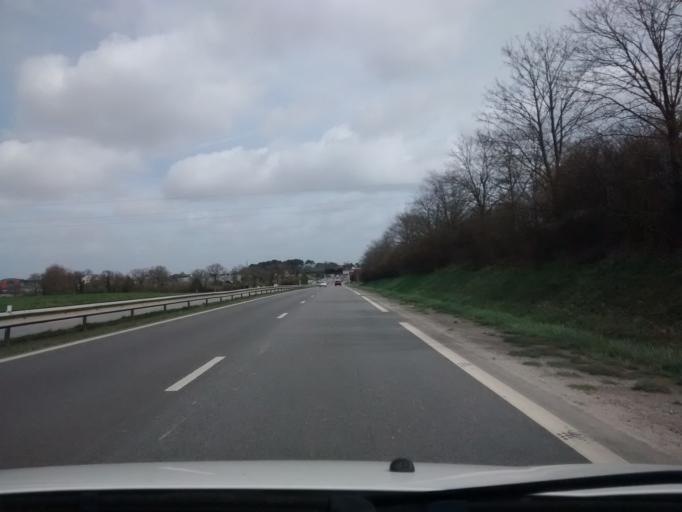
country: FR
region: Brittany
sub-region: Departement d'Ille-et-Vilaine
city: Bruz
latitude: 48.0502
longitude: -1.7474
